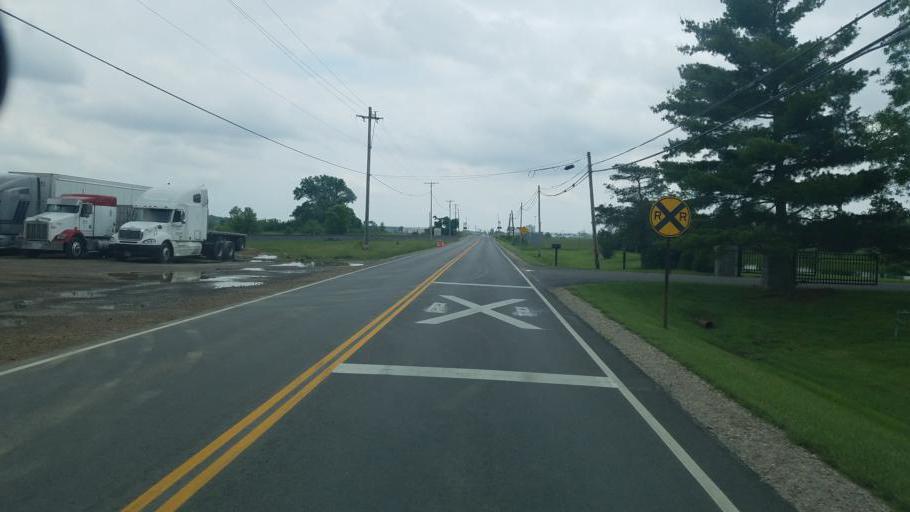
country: US
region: Ohio
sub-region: Union County
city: Marysville
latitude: 40.2281
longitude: -83.3454
